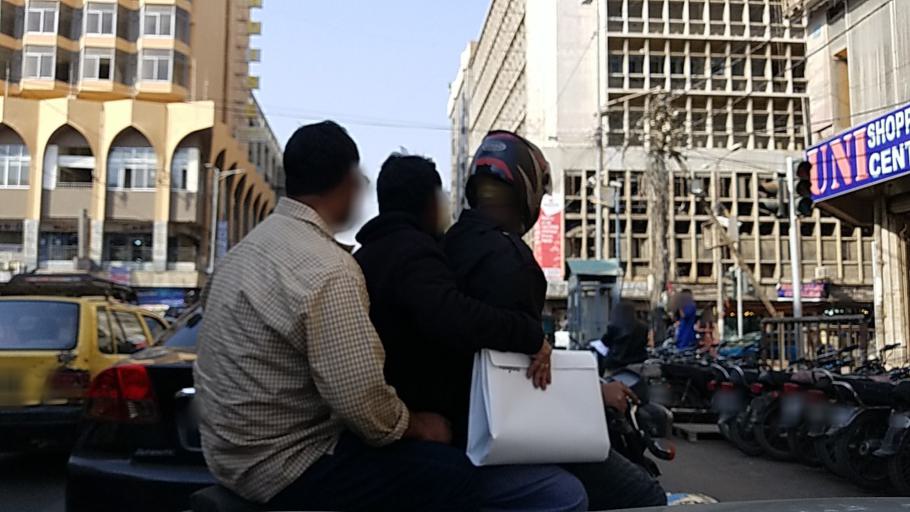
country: PK
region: Sindh
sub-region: Karachi District
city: Karachi
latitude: 24.8587
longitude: 67.0270
